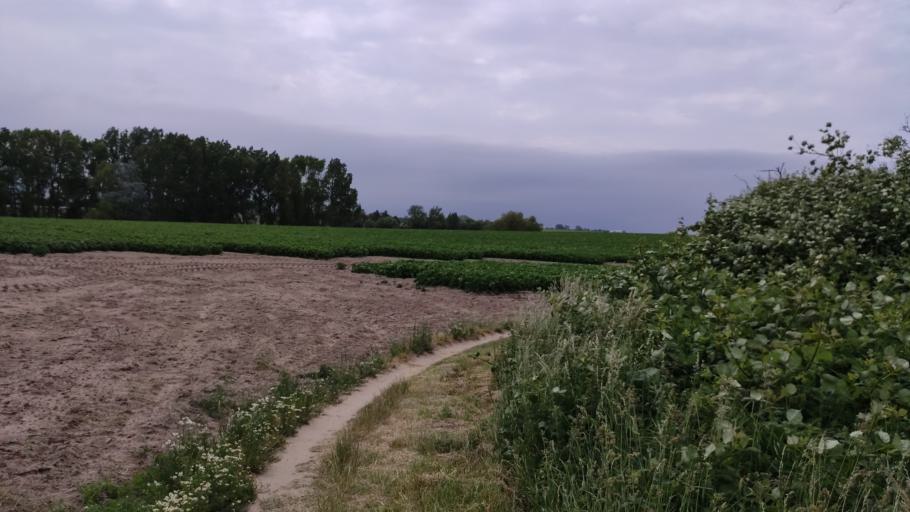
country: DE
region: Mecklenburg-Vorpommern
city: Bastorf
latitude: 54.1299
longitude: 11.6491
